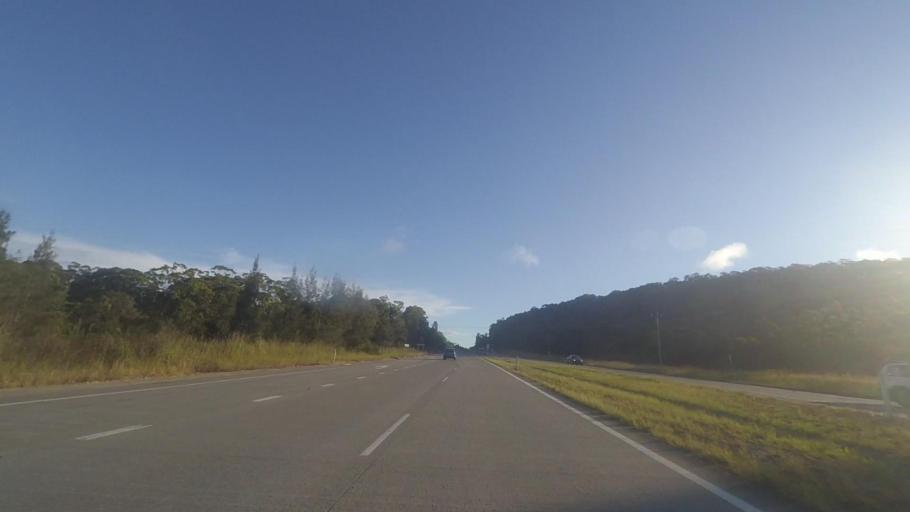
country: AU
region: New South Wales
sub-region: Great Lakes
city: Bulahdelah
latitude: -32.4673
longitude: 152.1961
